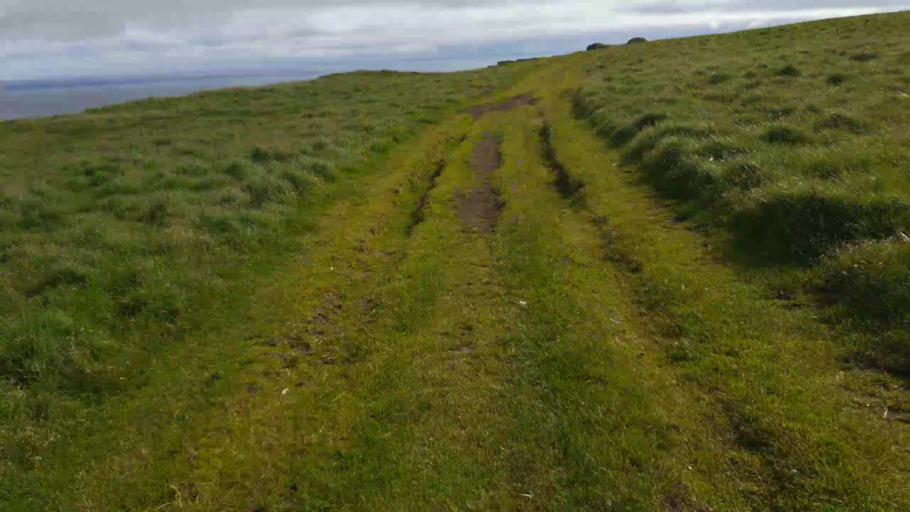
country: IS
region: Northeast
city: Dalvik
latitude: 66.5507
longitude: -17.9931
